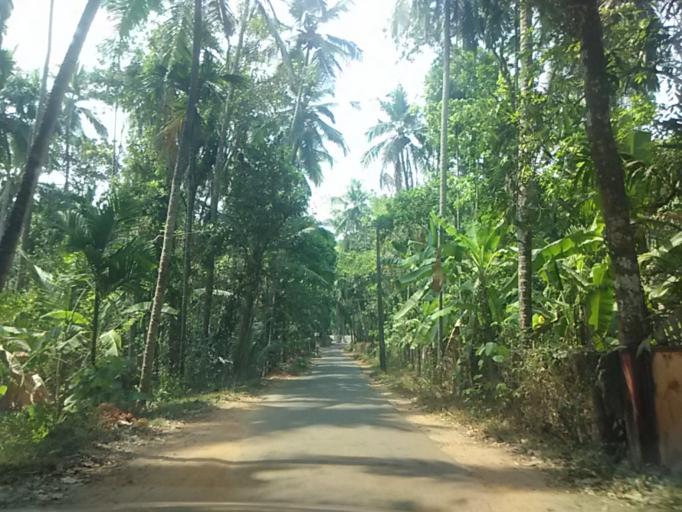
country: IN
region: Kerala
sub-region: Kozhikode
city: Naduvannur
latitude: 11.5370
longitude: 75.7571
